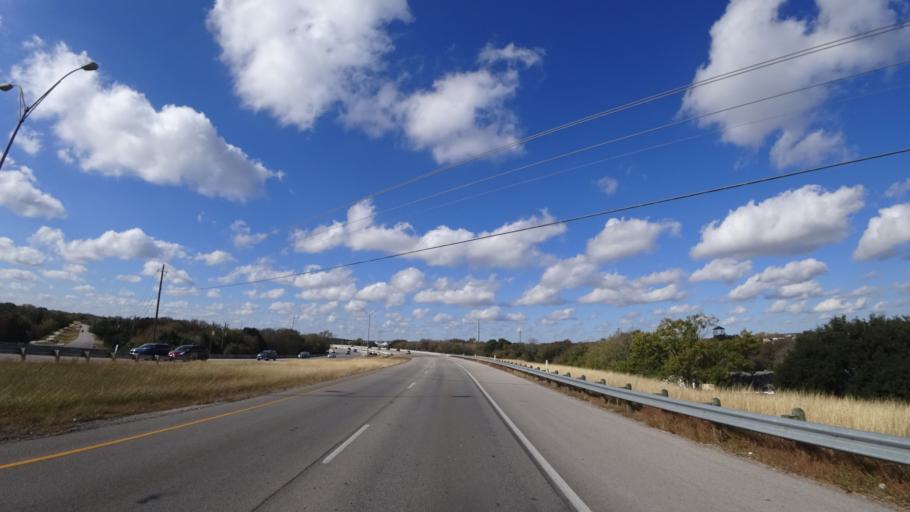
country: US
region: Texas
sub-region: Travis County
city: Shady Hollow
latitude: 30.2168
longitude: -97.8479
